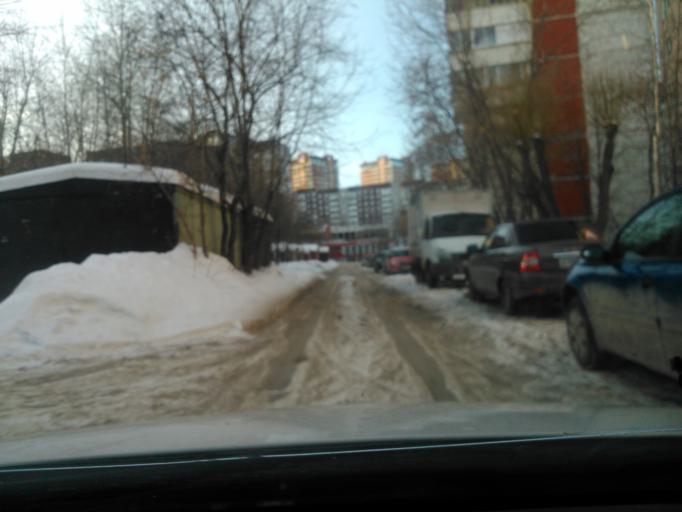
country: RU
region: Perm
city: Perm
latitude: 57.9994
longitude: 56.3095
